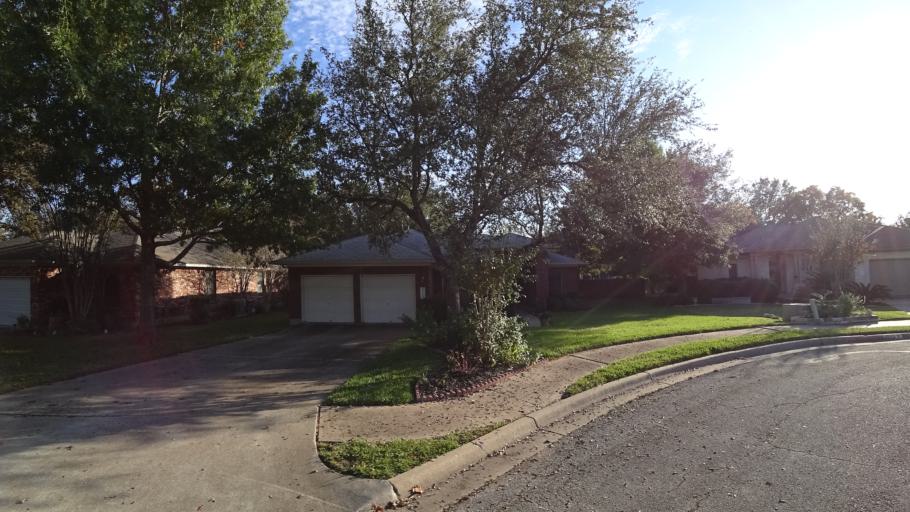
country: US
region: Texas
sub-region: Williamson County
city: Anderson Mill
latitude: 30.4456
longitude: -97.8022
